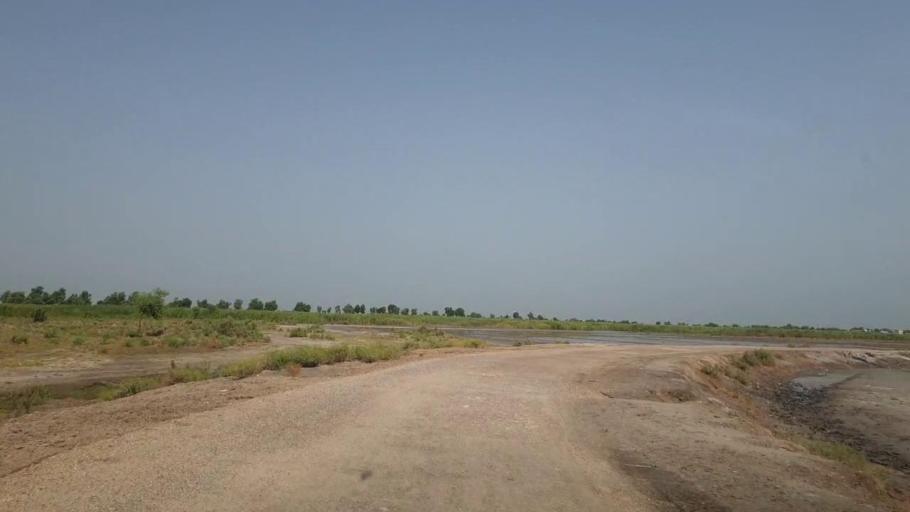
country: PK
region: Sindh
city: Sakrand
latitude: 26.2984
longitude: 68.2206
